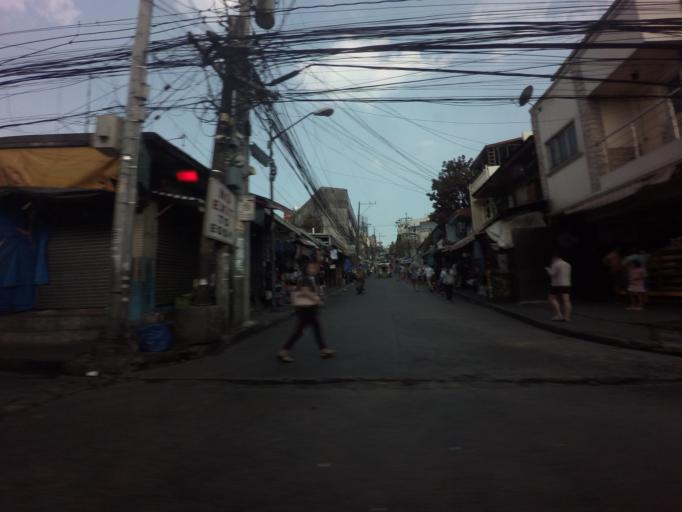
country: PH
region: Metro Manila
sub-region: Mandaluyong
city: Mandaluyong City
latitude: 14.5655
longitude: 121.0474
